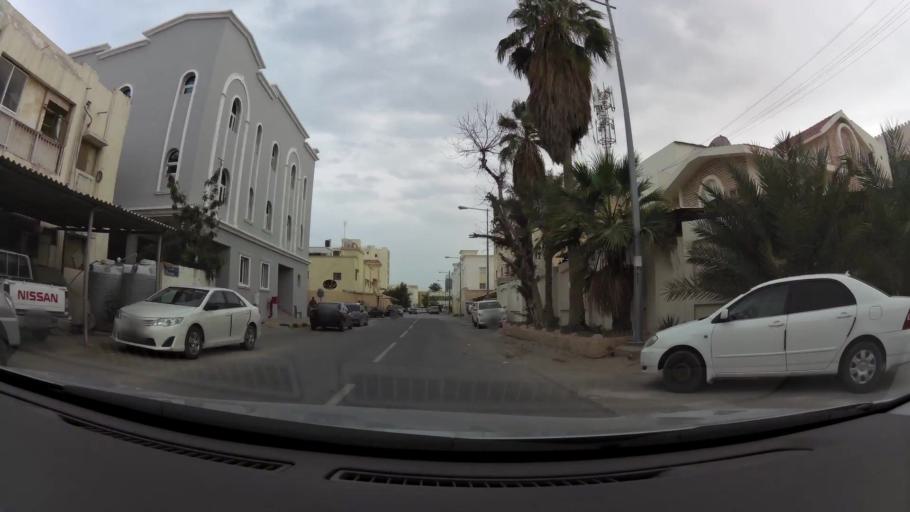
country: QA
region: Baladiyat ad Dawhah
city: Doha
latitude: 25.3166
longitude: 51.4933
